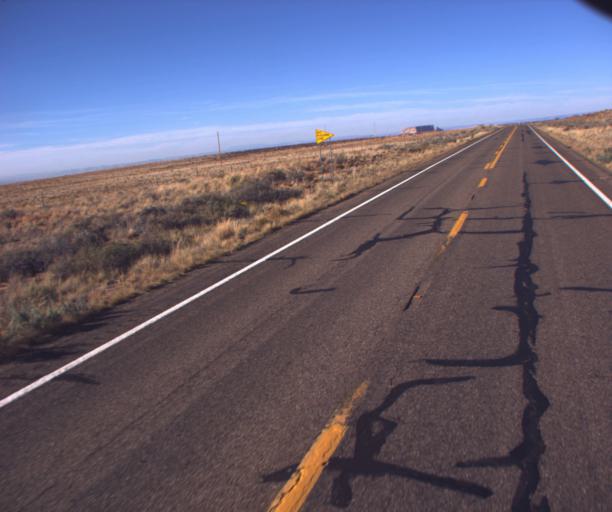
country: US
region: Arizona
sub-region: Coconino County
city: LeChee
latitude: 36.7511
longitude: -111.2848
